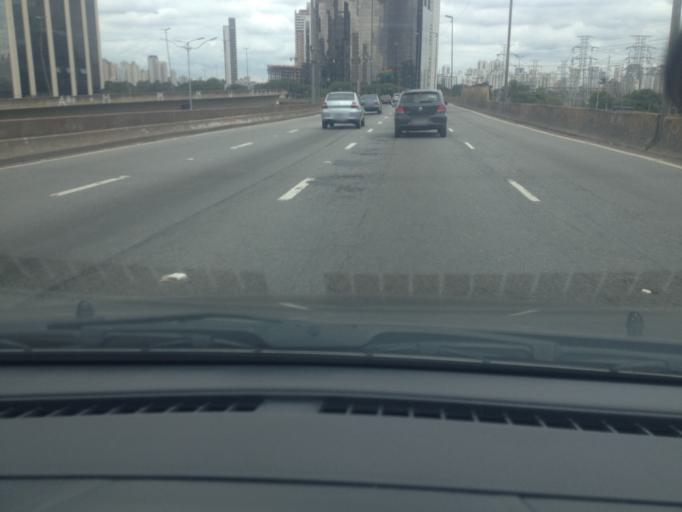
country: BR
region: Sao Paulo
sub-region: Sao Paulo
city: Sao Paulo
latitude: -23.5949
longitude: -46.6932
